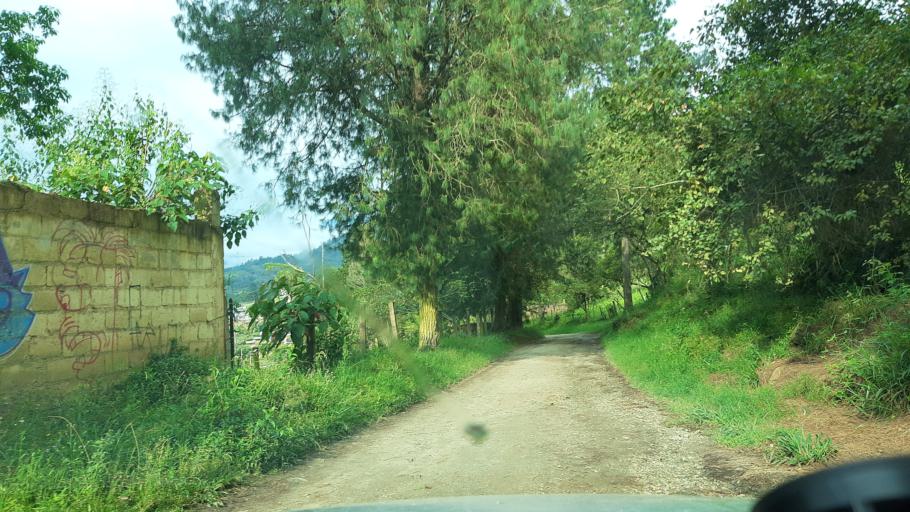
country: CO
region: Boyaca
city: Garagoa
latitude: 5.0739
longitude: -73.3628
